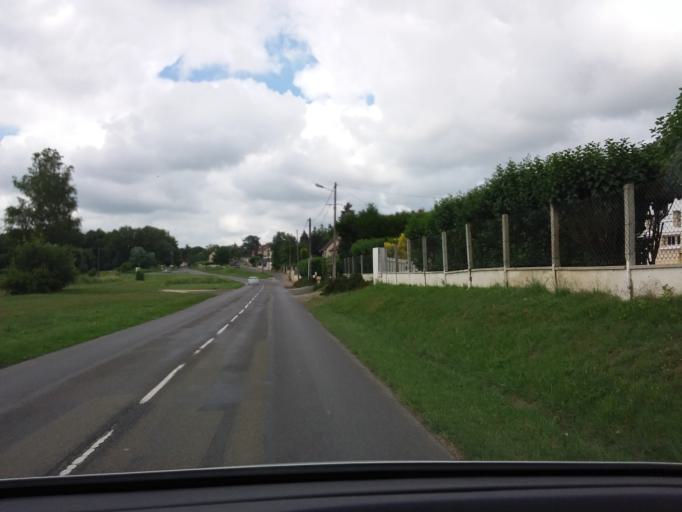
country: FR
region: Picardie
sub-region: Departement de l'Aisne
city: Vailly-sur-Aisne
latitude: 49.4013
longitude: 3.4760
